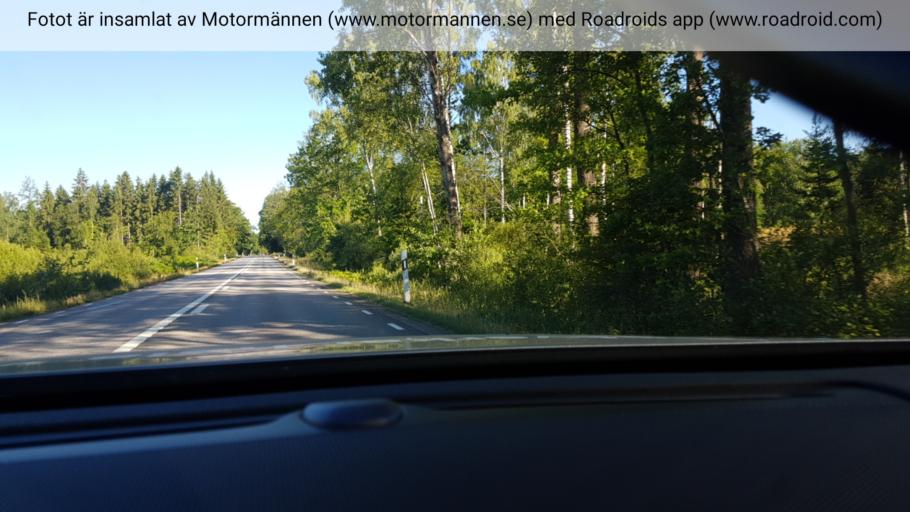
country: SE
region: Kronoberg
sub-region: Markaryds Kommun
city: Markaryd
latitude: 56.4122
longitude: 13.6363
